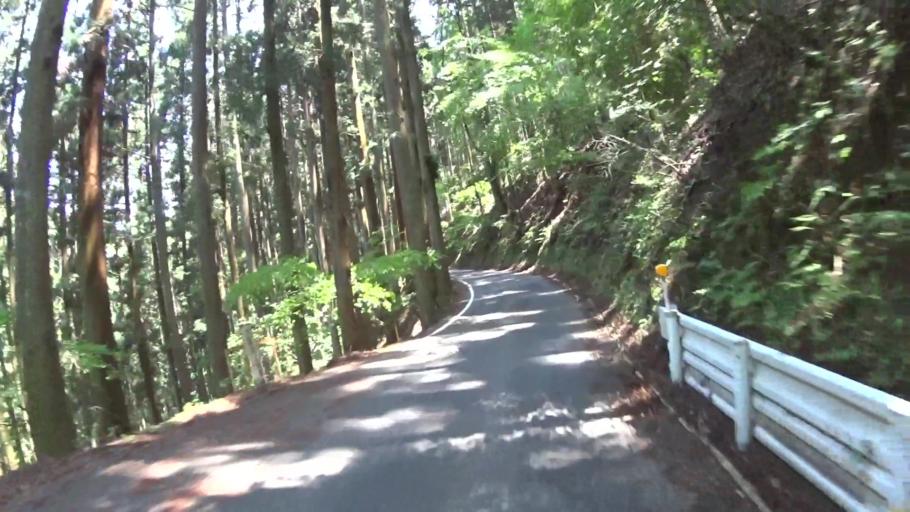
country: JP
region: Kyoto
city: Kameoka
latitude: 35.1226
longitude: 135.5846
